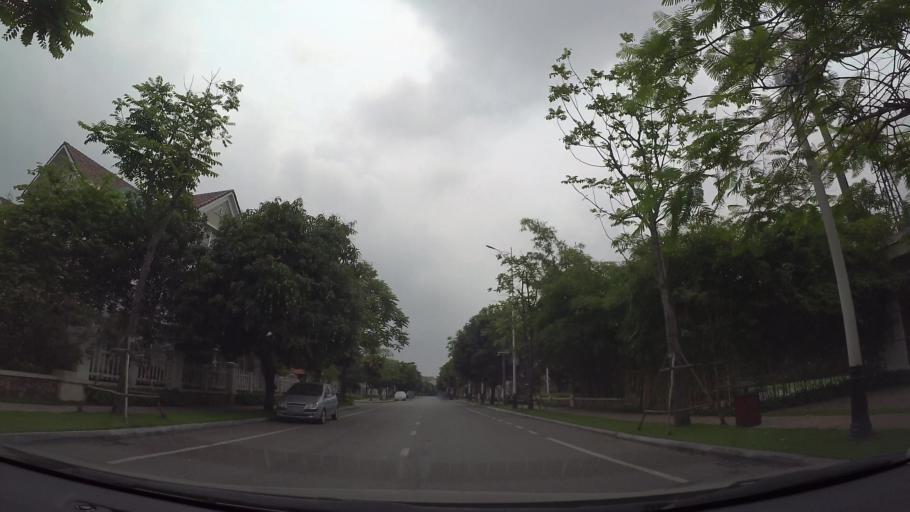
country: VN
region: Ha Noi
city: Trau Quy
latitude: 21.0410
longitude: 105.9179
